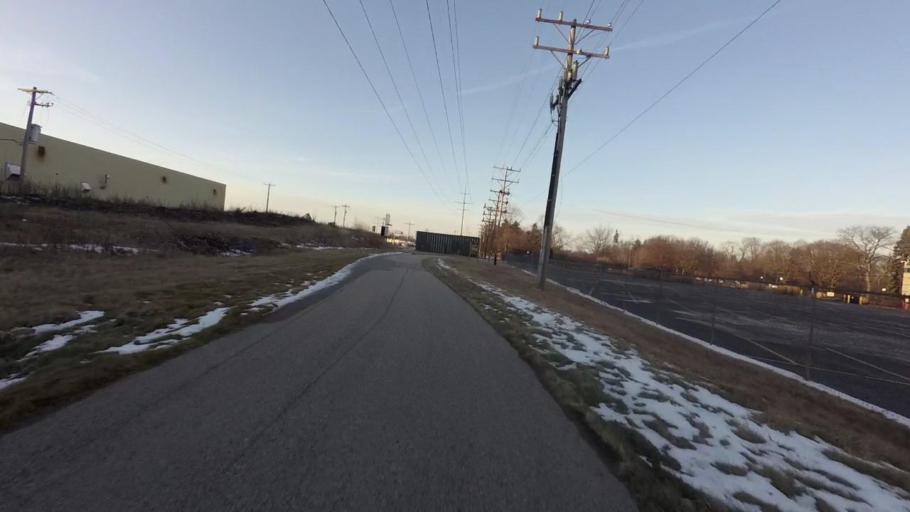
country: US
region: Wisconsin
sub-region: Milwaukee County
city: Brown Deer
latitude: 43.1469
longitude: -87.9538
